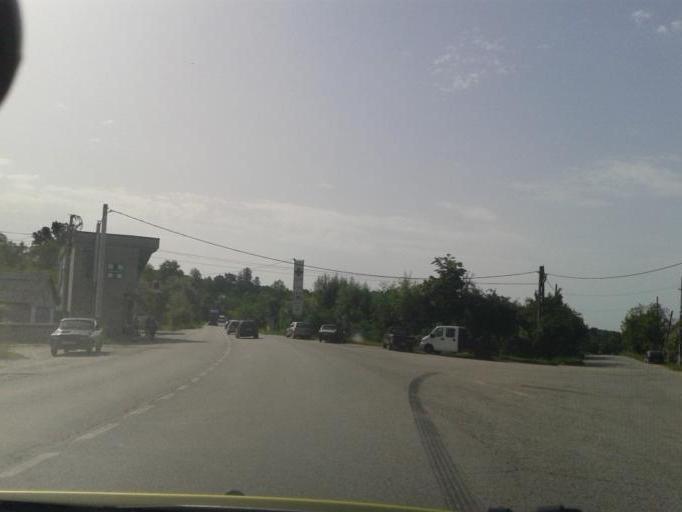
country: RO
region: Valcea
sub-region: Comuna Pietrari
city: Pietrari
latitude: 45.1018
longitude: 24.1228
